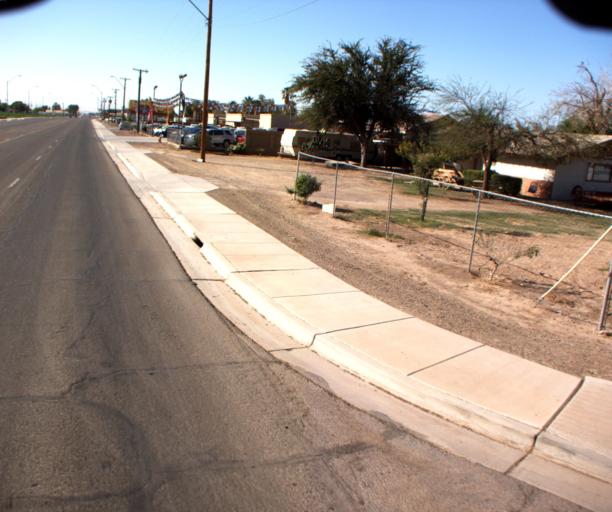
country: US
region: Arizona
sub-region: Yuma County
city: San Luis
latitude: 32.5617
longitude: -114.7848
